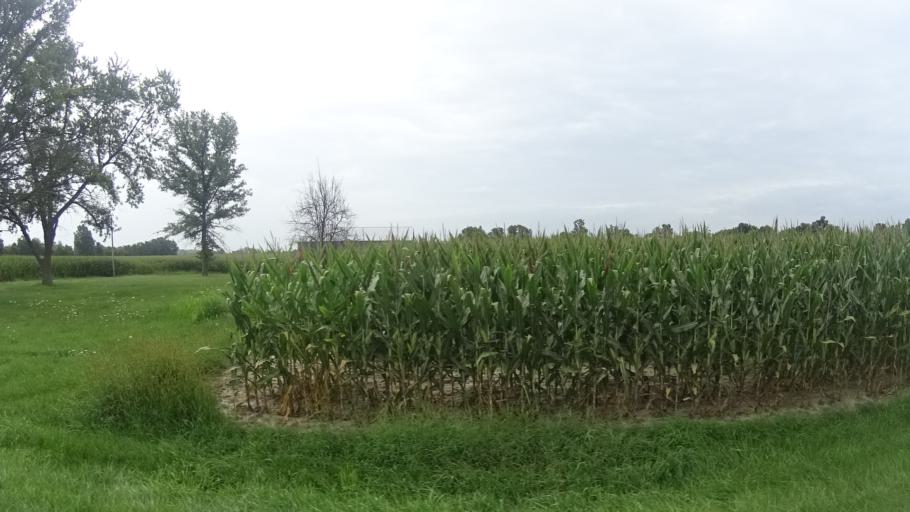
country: US
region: Indiana
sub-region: Madison County
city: Edgewood
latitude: 40.1017
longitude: -85.7770
